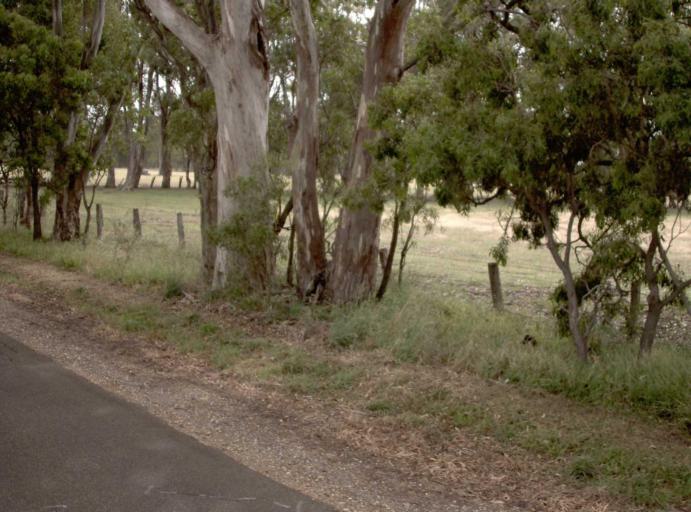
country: AU
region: Victoria
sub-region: Wellington
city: Sale
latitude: -37.8675
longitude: 147.0679
